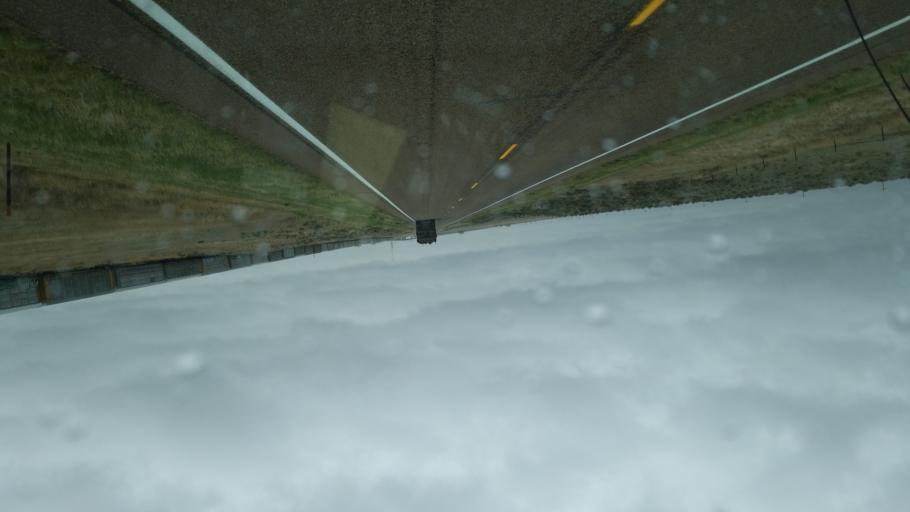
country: US
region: Colorado
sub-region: Kiowa County
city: Eads
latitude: 38.7709
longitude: -102.7597
